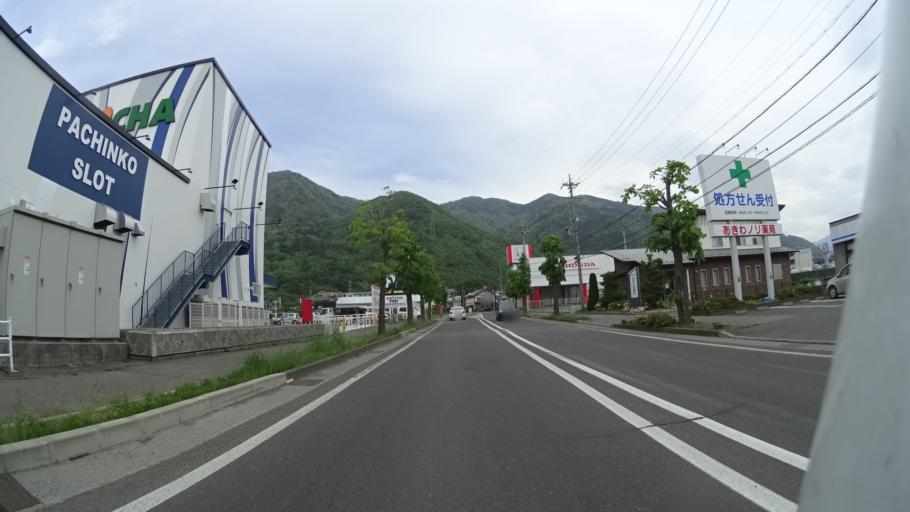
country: JP
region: Nagano
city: Ueda
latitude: 36.4138
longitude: 138.2249
